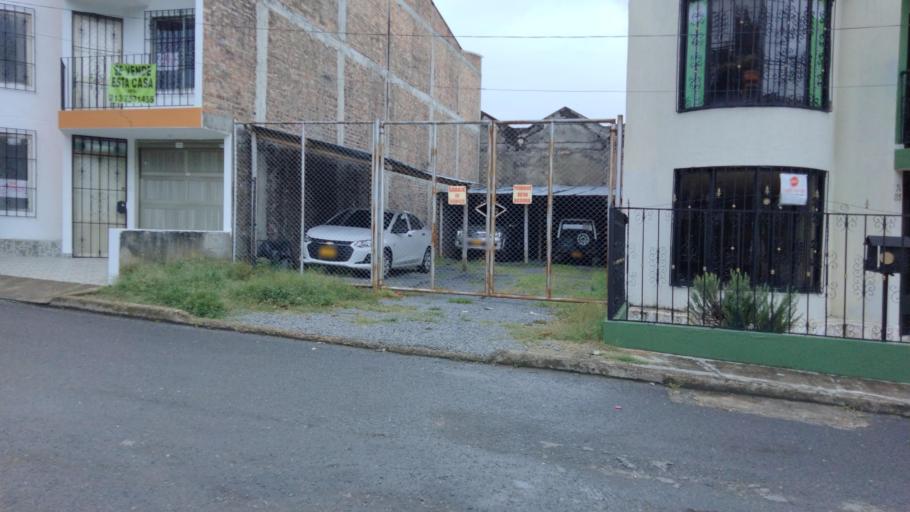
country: CO
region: Cauca
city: Popayan
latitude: 2.4584
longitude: -76.5912
